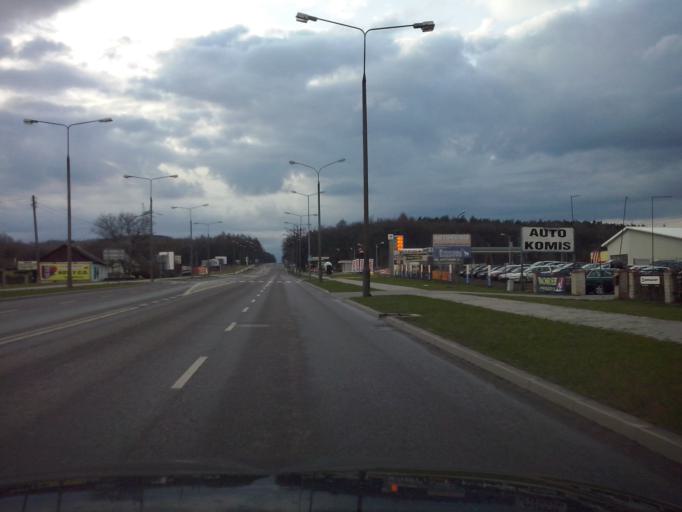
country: PL
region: Lublin Voivodeship
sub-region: Chelm
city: Chelm
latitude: 51.1481
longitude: 23.4315
